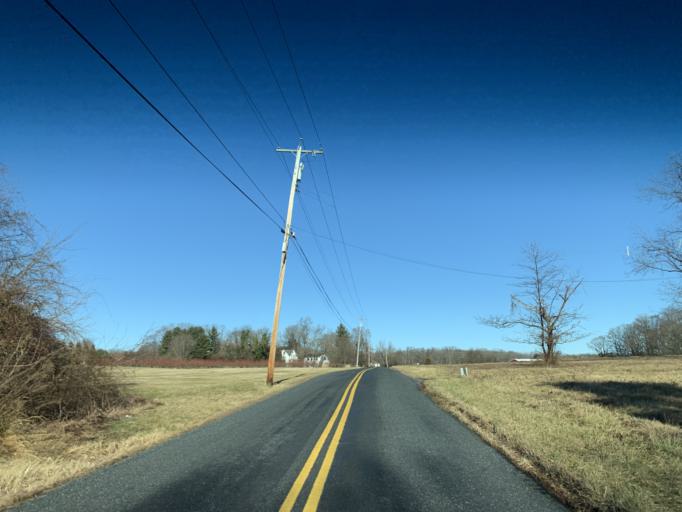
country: US
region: Maryland
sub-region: Harford County
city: Riverside
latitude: 39.5393
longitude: -76.2363
